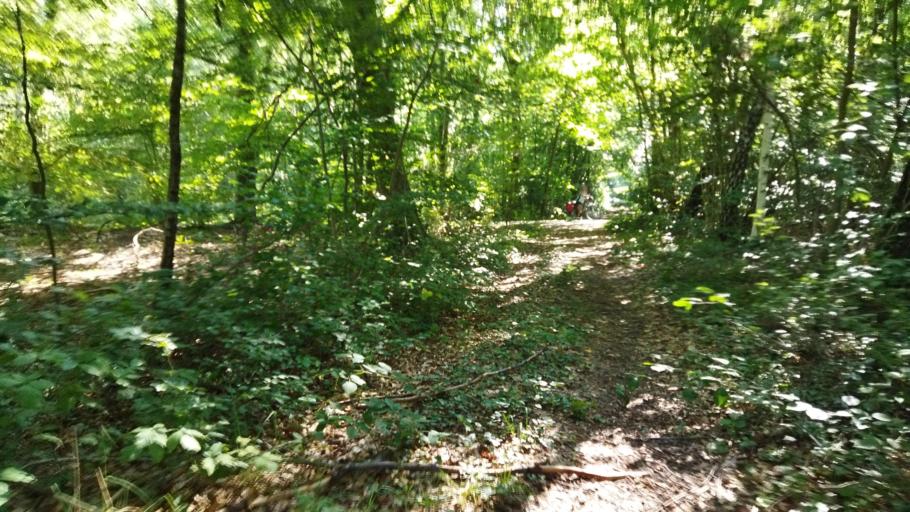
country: DE
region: Lower Saxony
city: Laar
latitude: 52.3721
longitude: 8.2444
